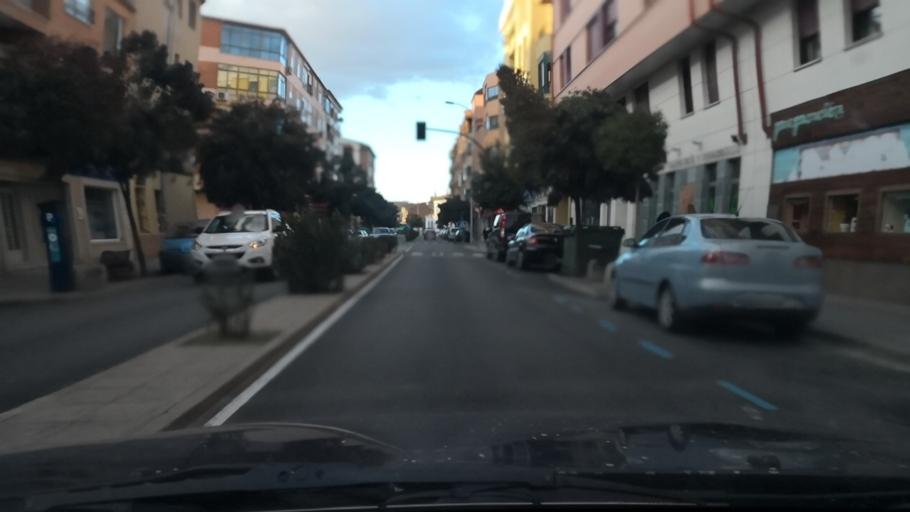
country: ES
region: Castille and Leon
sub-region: Provincia de Valladolid
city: Medina del Campo
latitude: 41.3077
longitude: -4.9117
